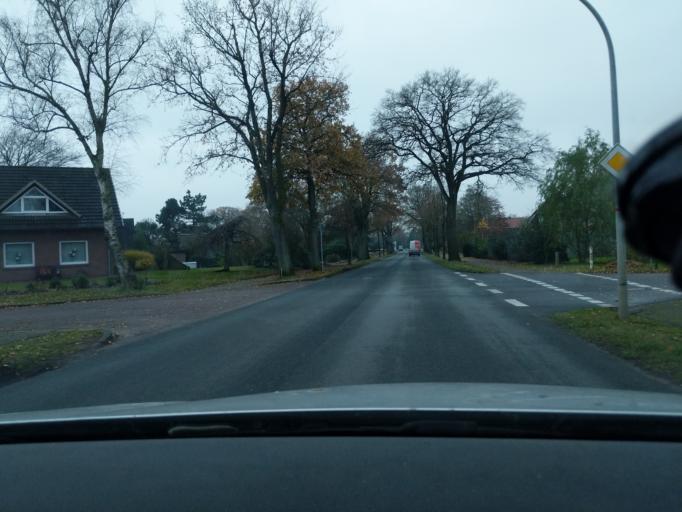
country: DE
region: Lower Saxony
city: Heeslingen
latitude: 53.3200
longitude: 9.3414
